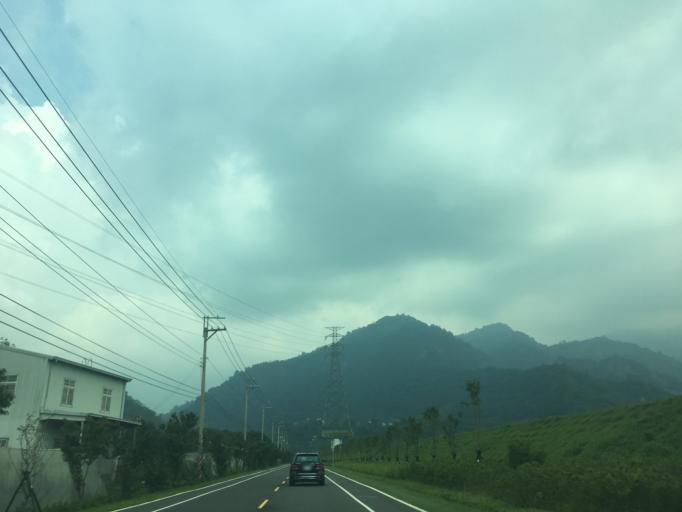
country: TW
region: Taiwan
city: Fengyuan
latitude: 24.2953
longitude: 120.8968
